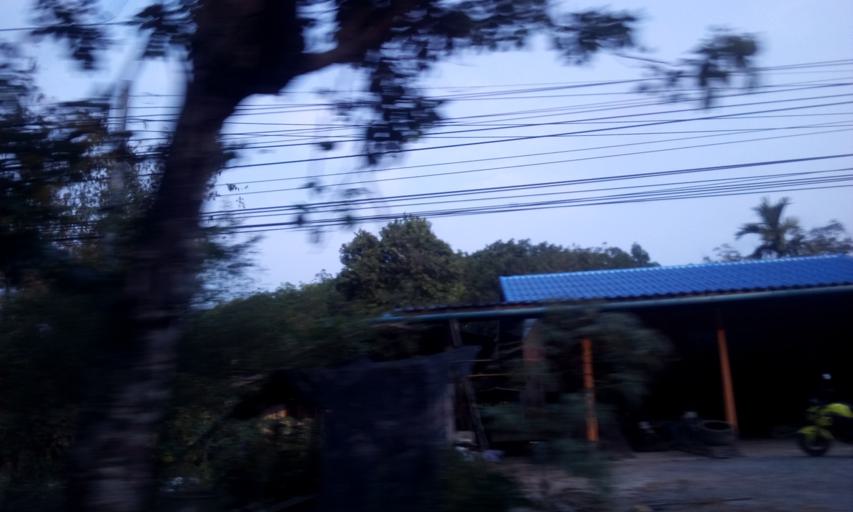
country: TH
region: Trat
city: Laem Ngop
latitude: 12.2830
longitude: 102.3100
